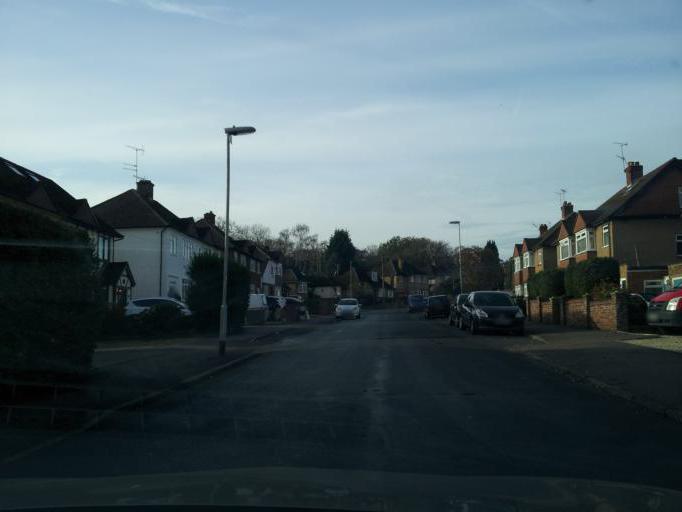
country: GB
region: England
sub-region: Greater London
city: Harefield
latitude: 51.6197
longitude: -0.5135
